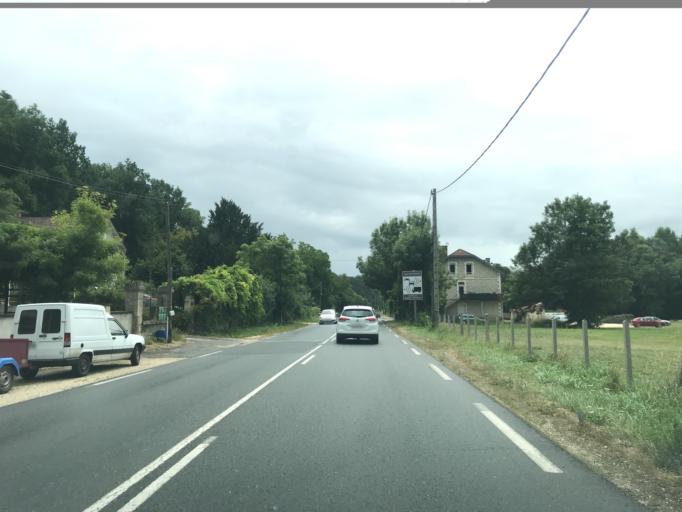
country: FR
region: Aquitaine
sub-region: Departement de la Dordogne
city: Chancelade
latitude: 45.2407
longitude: 0.6852
